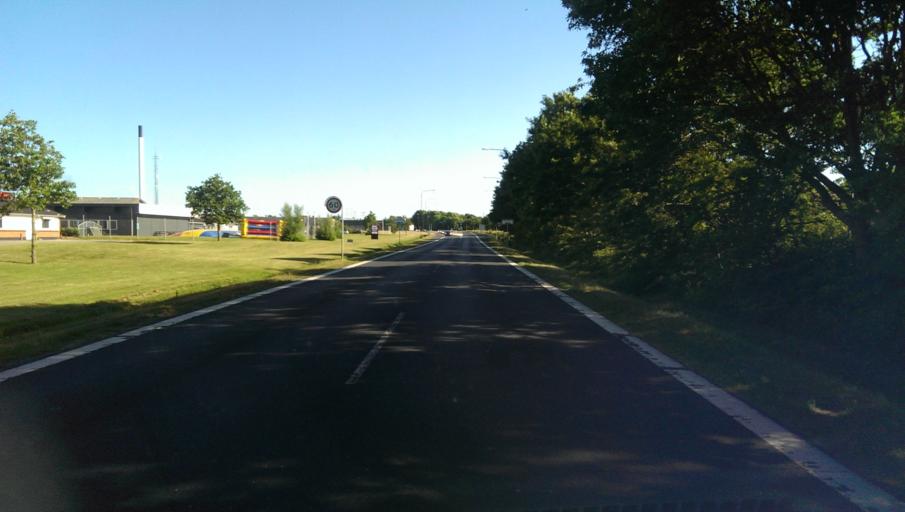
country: DK
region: South Denmark
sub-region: Esbjerg Kommune
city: Esbjerg
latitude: 55.5069
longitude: 8.4055
